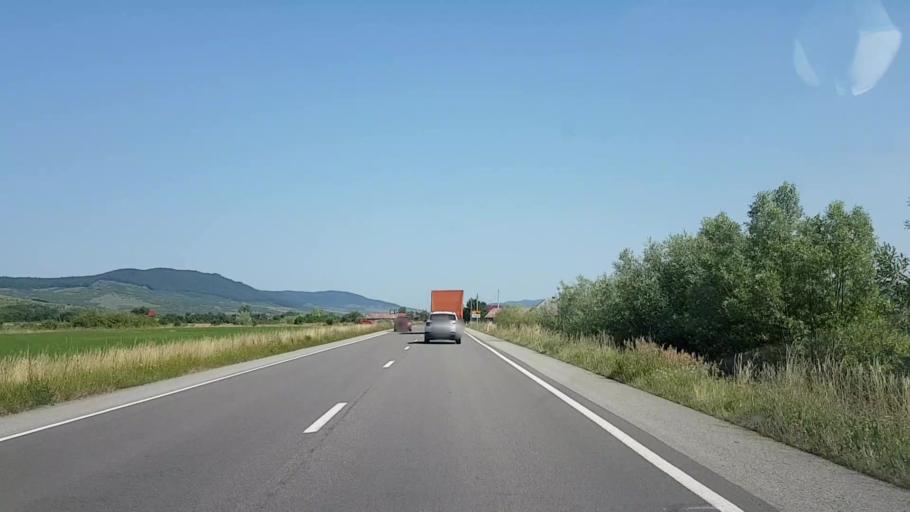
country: RO
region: Bistrita-Nasaud
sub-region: Comuna Sieu-Odorhei
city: Sieu-Odorhei
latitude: 47.1205
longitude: 24.3282
